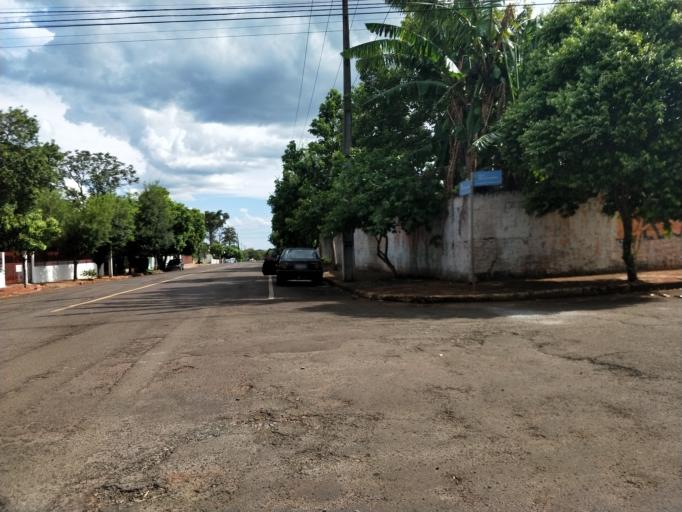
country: BR
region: Parana
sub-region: Marechal Candido Rondon
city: Marechal Candido Rondon
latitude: -24.5609
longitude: -54.0544
